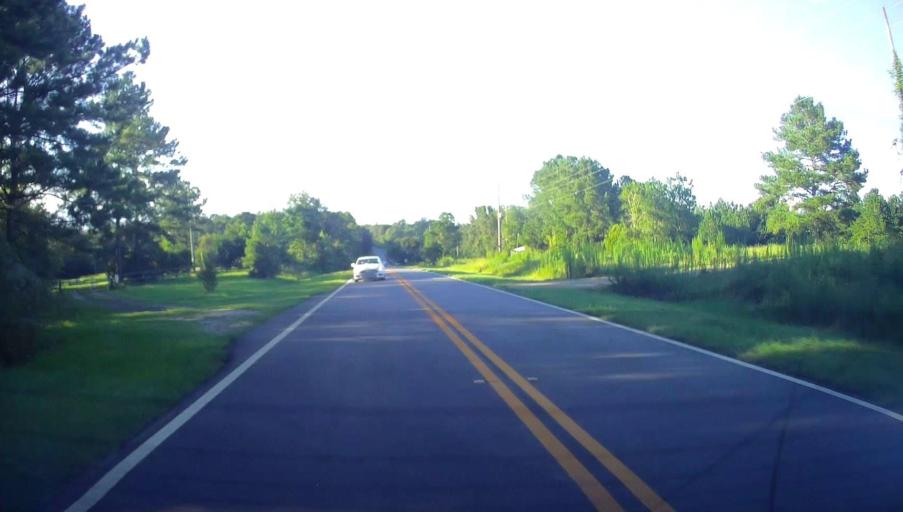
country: US
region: Georgia
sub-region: Pulaski County
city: Hawkinsville
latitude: 32.2973
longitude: -83.4498
